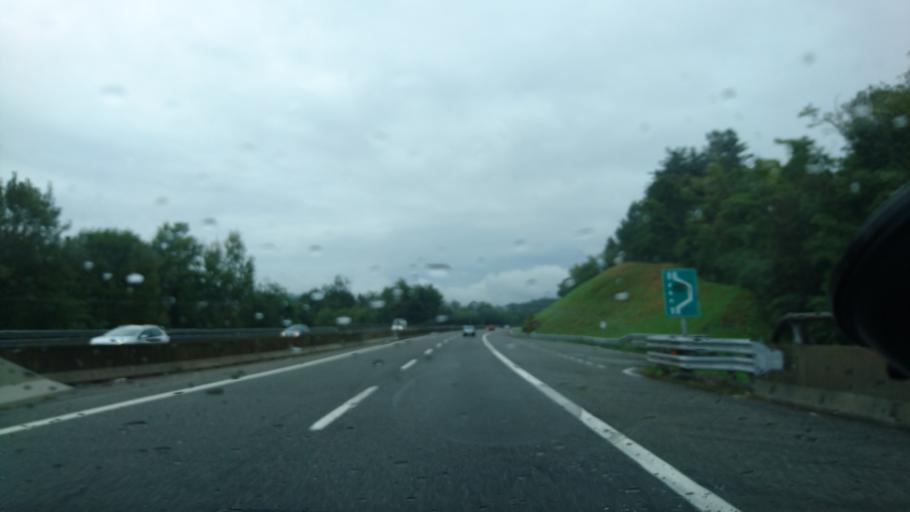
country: IT
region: Piedmont
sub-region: Provincia di Novara
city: Pisano
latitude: 45.7870
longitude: 8.5135
